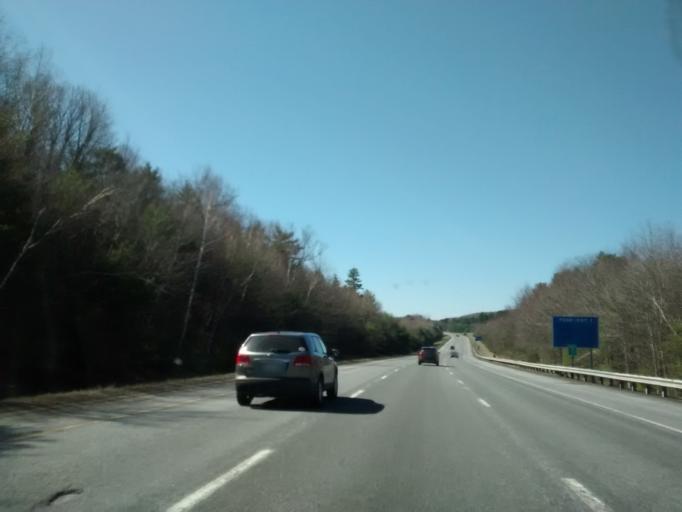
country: US
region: Massachusetts
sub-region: Worcester County
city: Sturbridge
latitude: 42.0761
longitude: -72.1013
